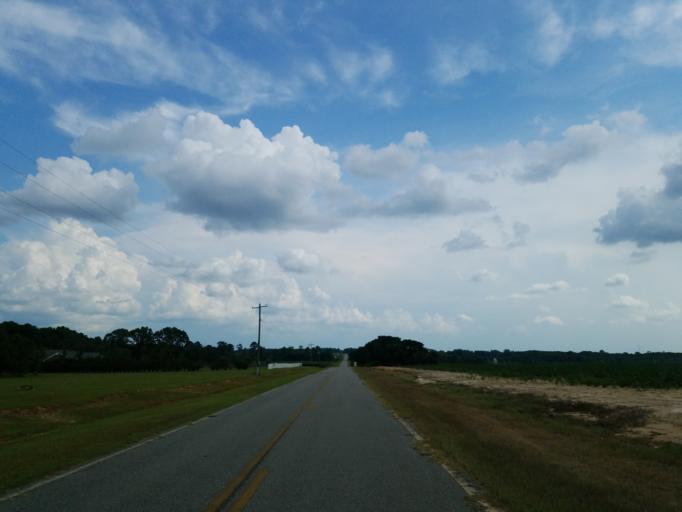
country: US
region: Georgia
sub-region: Dooly County
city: Unadilla
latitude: 32.2781
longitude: -83.7189
